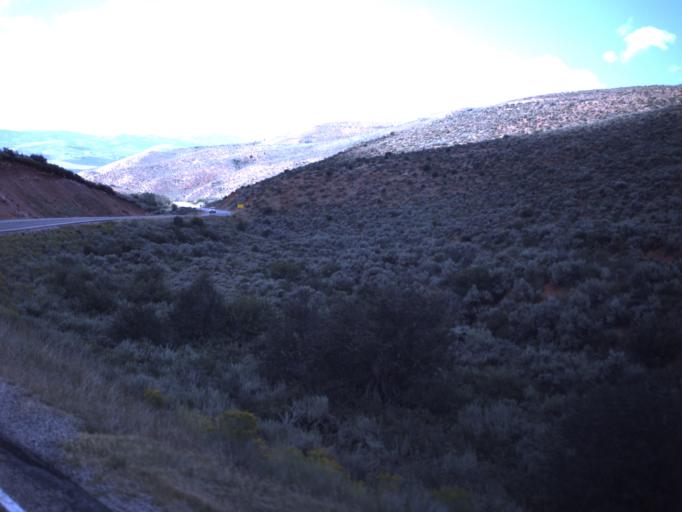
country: US
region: Utah
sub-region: Rich County
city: Randolph
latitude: 41.8084
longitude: -111.2591
